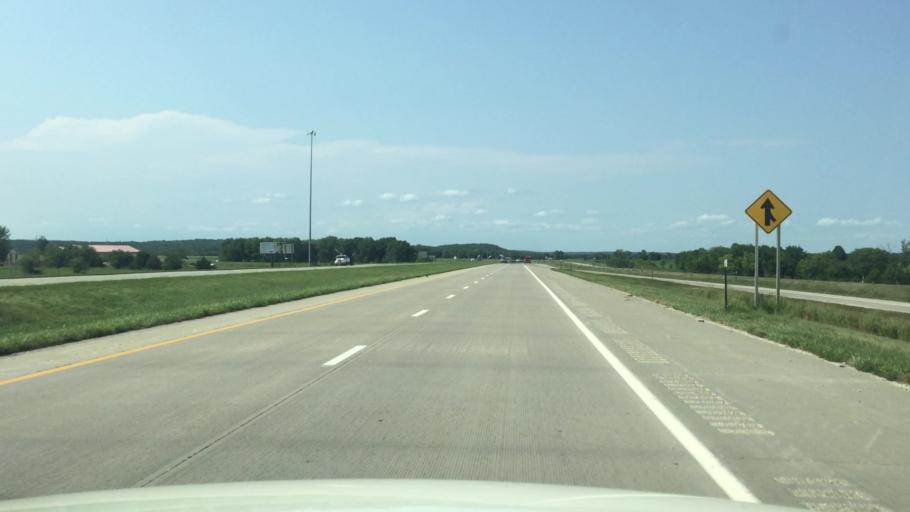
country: US
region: Kansas
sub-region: Linn County
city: Pleasanton
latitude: 38.1829
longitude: -94.7004
